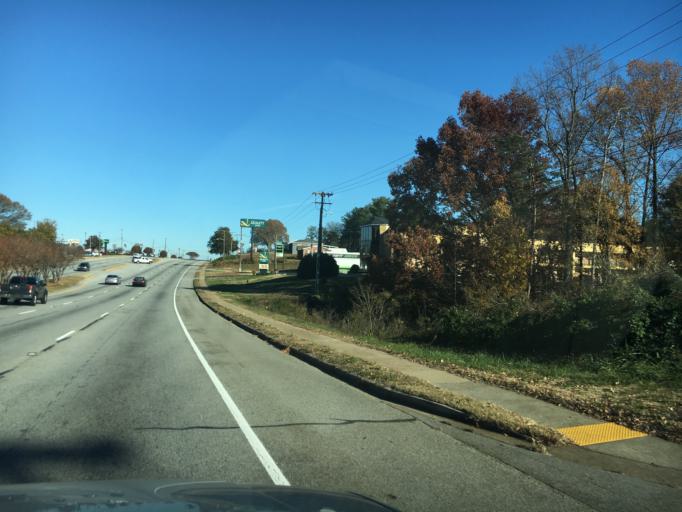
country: US
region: South Carolina
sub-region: Greenville County
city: Greer
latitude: 34.9476
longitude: -82.2426
